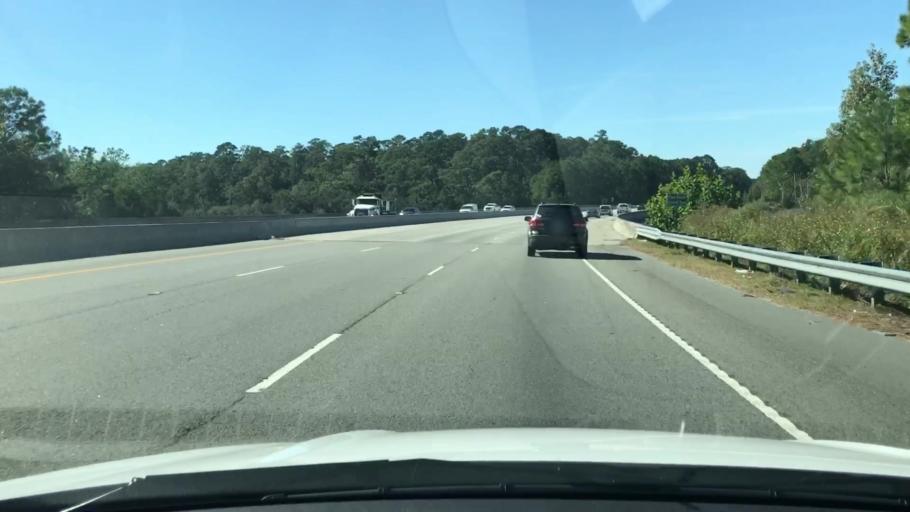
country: US
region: South Carolina
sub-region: Beaufort County
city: Bluffton
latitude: 32.2893
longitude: -80.9278
